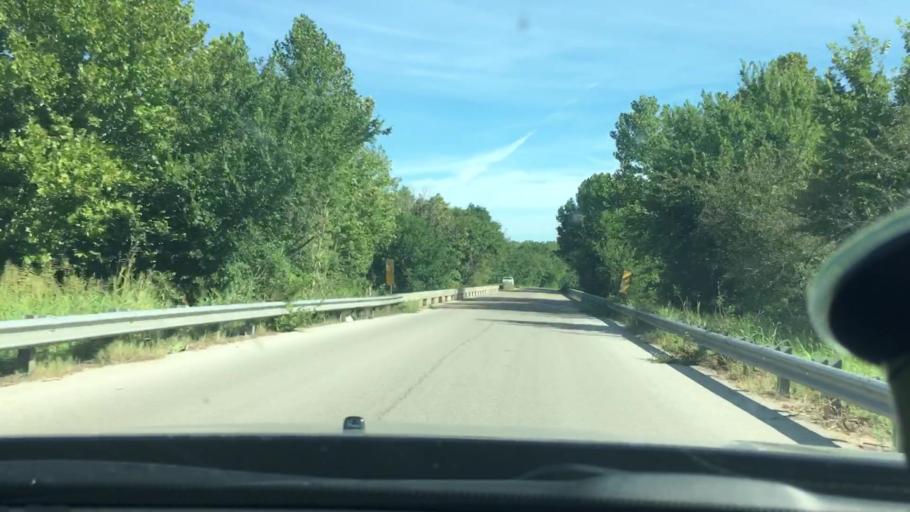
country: US
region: Oklahoma
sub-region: Carter County
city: Lone Grove
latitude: 34.2836
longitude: -97.2827
